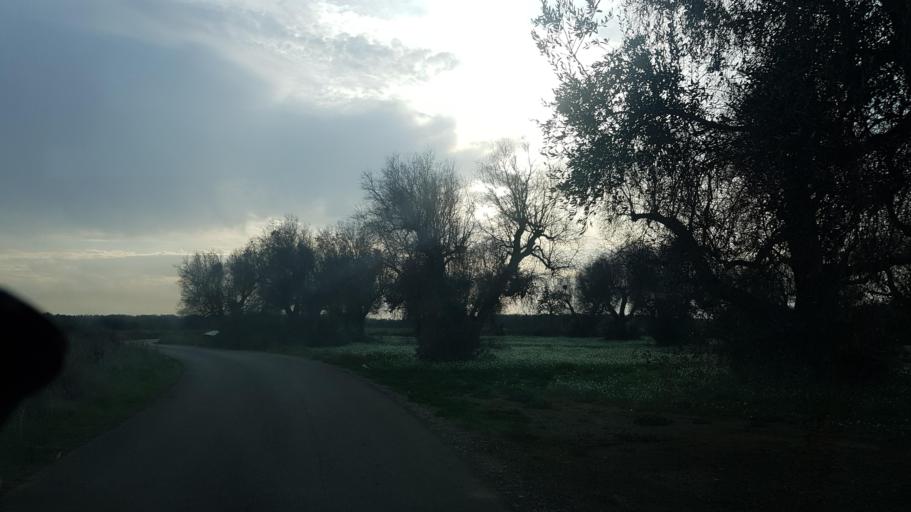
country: IT
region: Apulia
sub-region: Provincia di Brindisi
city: Mesagne
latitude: 40.5218
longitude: 17.8288
